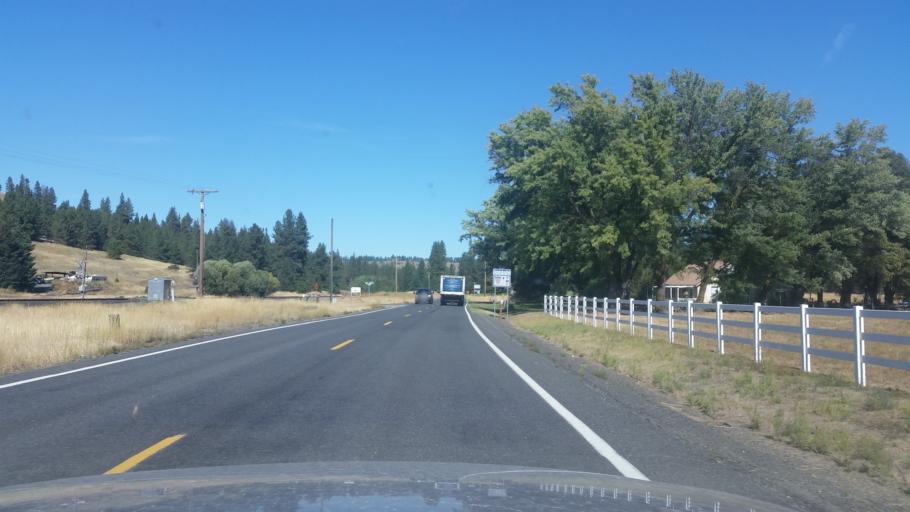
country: US
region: Washington
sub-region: Spokane County
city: Spokane
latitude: 47.5940
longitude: -117.4477
